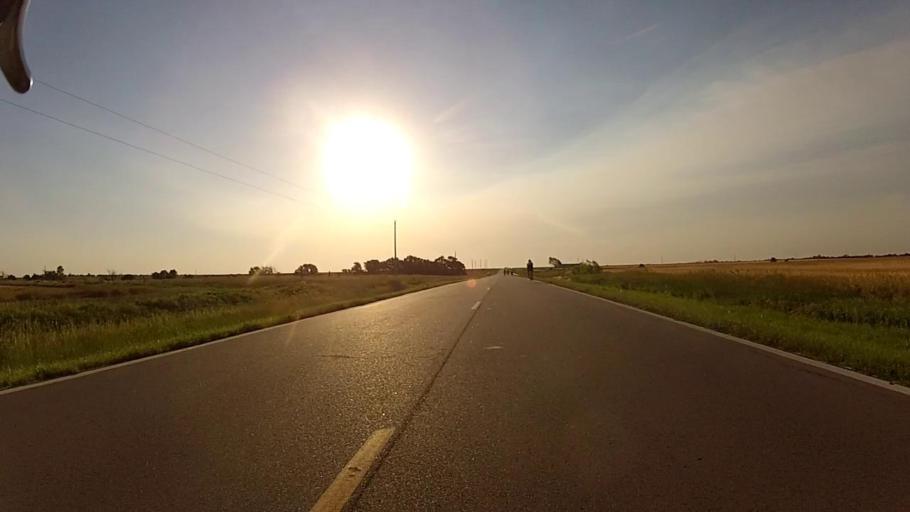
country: US
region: Kansas
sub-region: Harper County
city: Anthony
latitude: 37.1541
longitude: -97.8255
